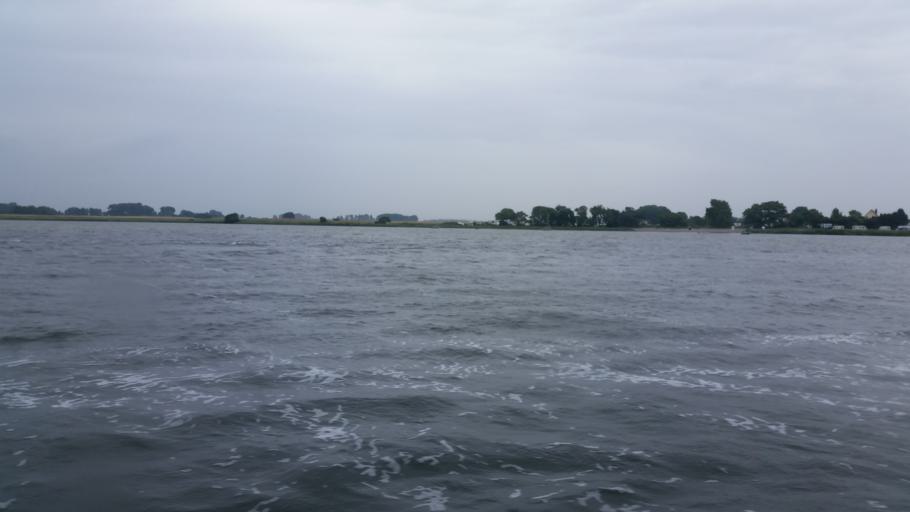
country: DE
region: Mecklenburg-Vorpommern
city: Hiddensee
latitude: 54.5176
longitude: 13.1578
